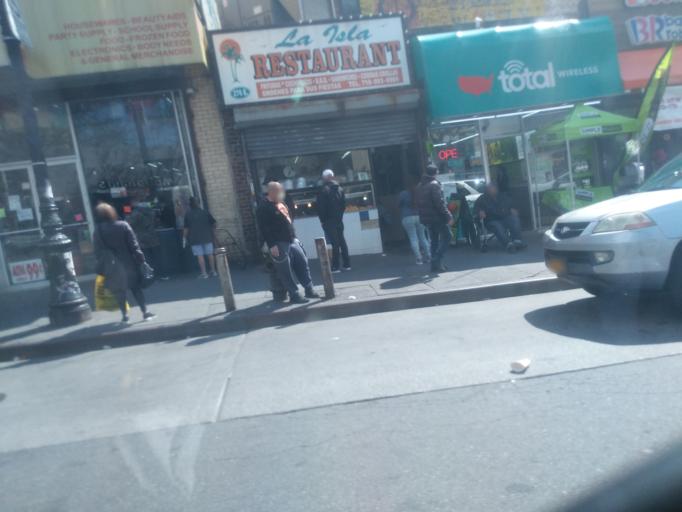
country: US
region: New York
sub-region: New York County
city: Inwood
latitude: 40.8172
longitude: -73.9225
